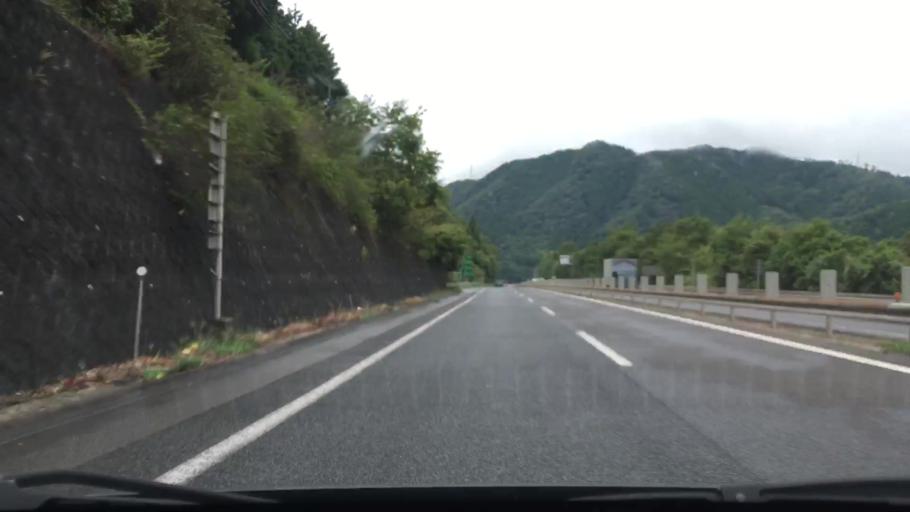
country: JP
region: Hiroshima
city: Hiroshima-shi
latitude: 34.5346
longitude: 132.4419
